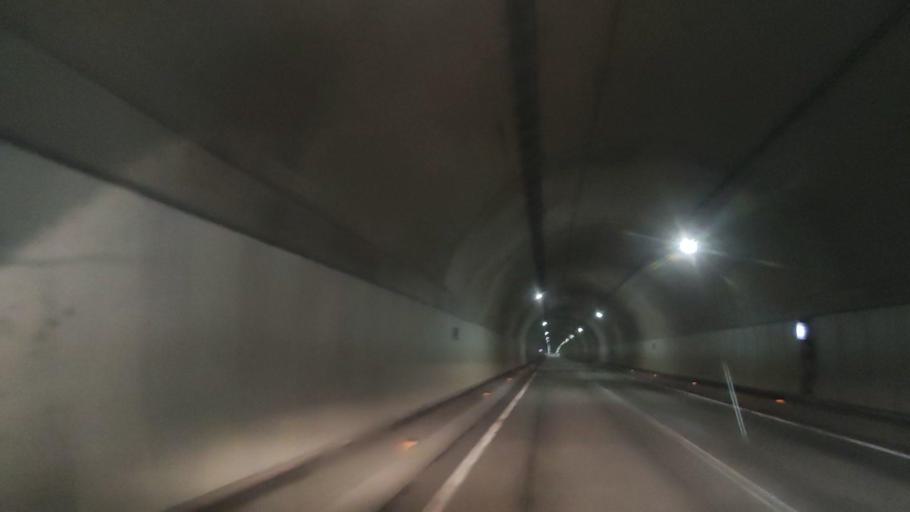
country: JP
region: Hokkaido
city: Date
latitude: 42.5534
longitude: 141.0760
